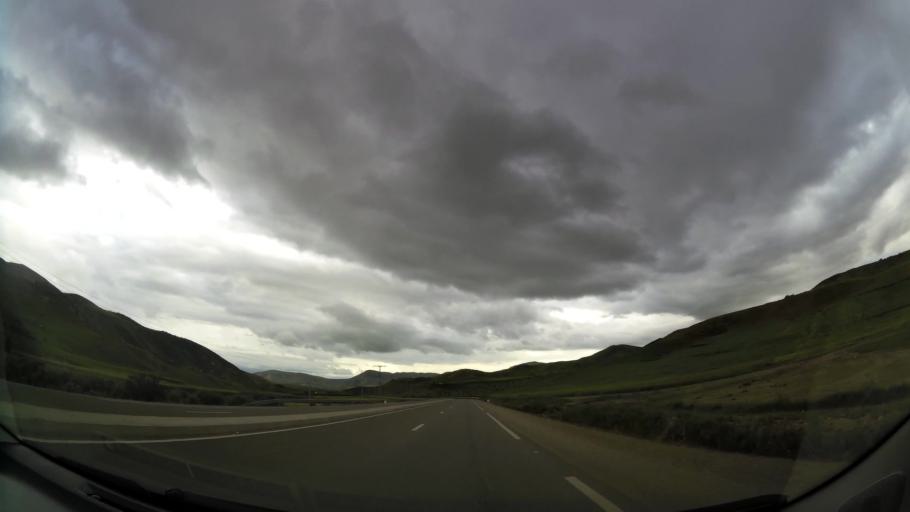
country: MA
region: Taza-Al Hoceima-Taounate
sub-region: Taza
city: Taza
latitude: 34.3363
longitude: -3.9418
